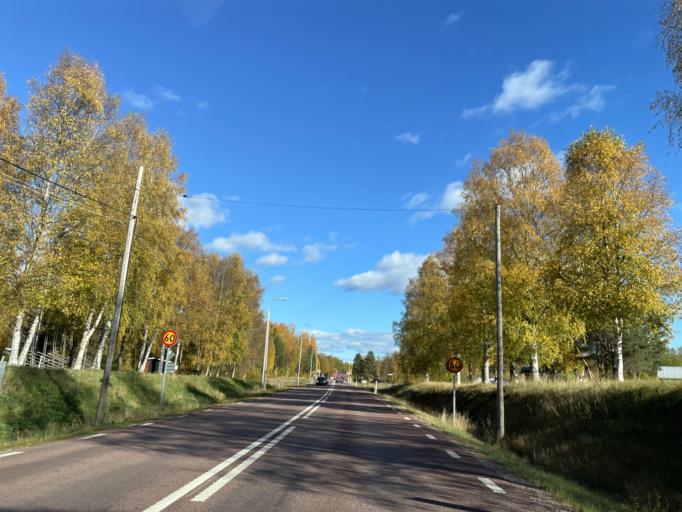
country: SE
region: Dalarna
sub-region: Malung-Saelens kommun
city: Malung
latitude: 60.7044
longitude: 13.6708
